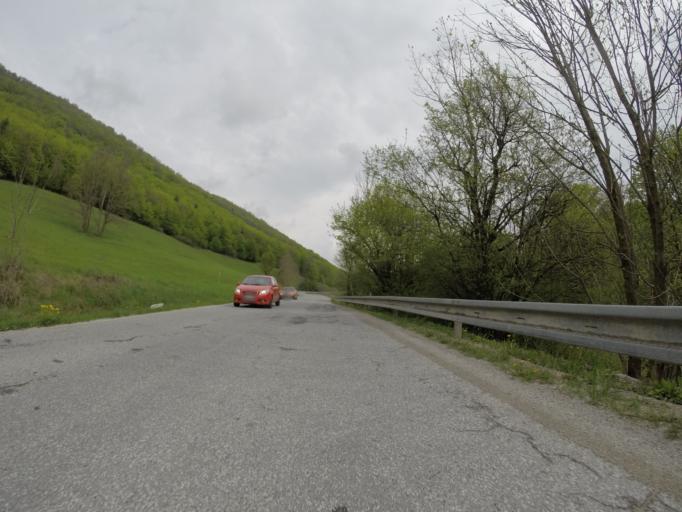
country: SK
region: Banskobystricky
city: Tisovec
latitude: 48.6964
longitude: 19.9768
